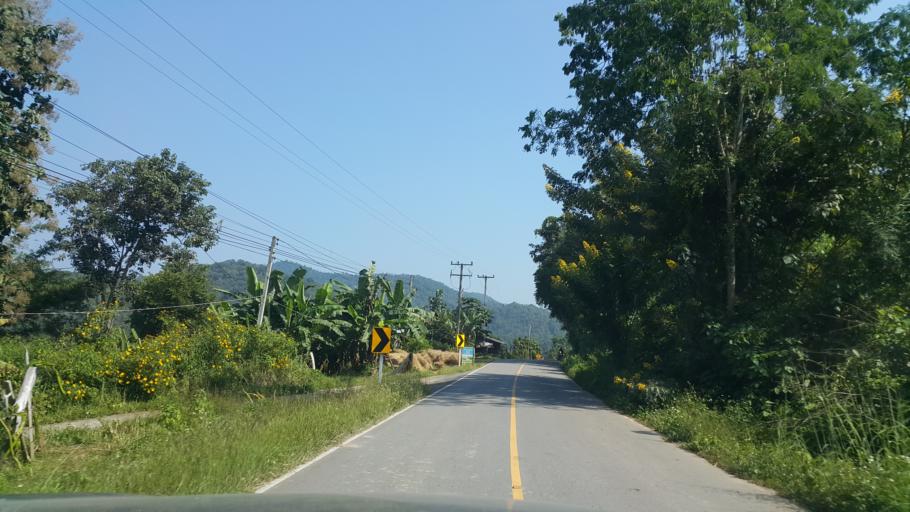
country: TH
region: Chiang Mai
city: Samoeng
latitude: 18.8645
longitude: 98.6389
